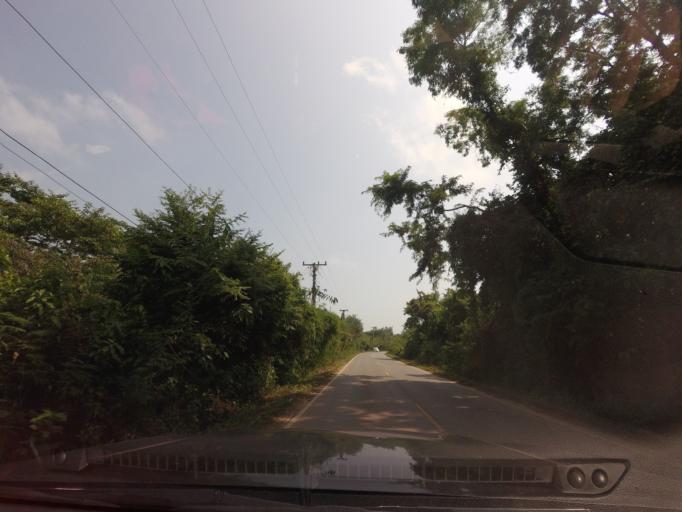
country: TH
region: Nan
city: Nan
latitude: 18.7735
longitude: 100.7353
